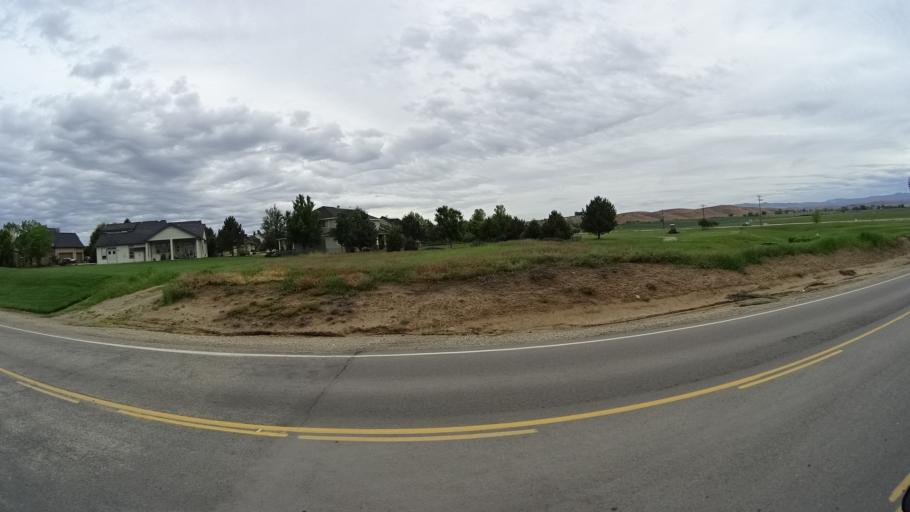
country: US
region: Idaho
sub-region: Ada County
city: Star
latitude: 43.7209
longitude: -116.4600
